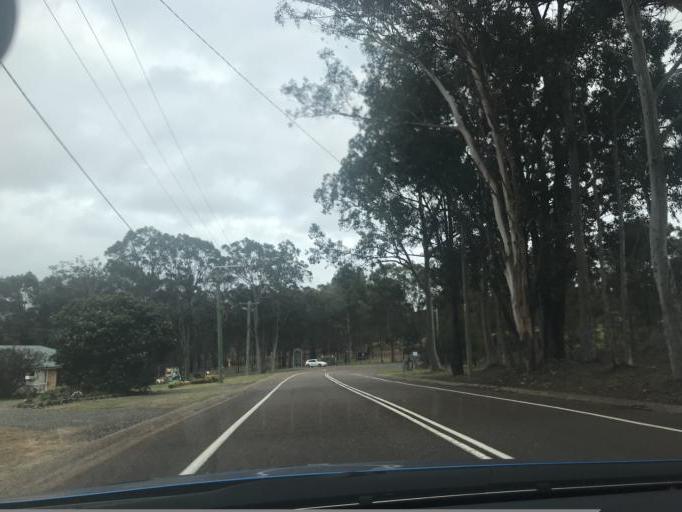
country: AU
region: New South Wales
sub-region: Cessnock
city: Cessnock
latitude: -32.8284
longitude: 151.3238
